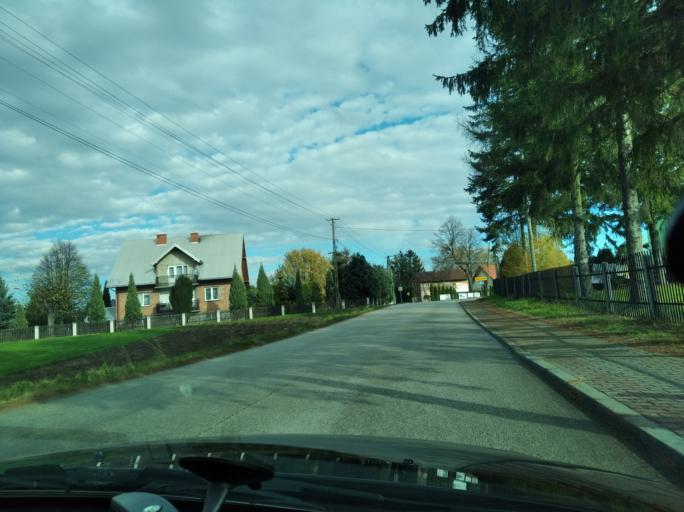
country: PL
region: Subcarpathian Voivodeship
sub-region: Powiat debicki
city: Brzeznica
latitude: 50.0914
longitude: 21.5223
